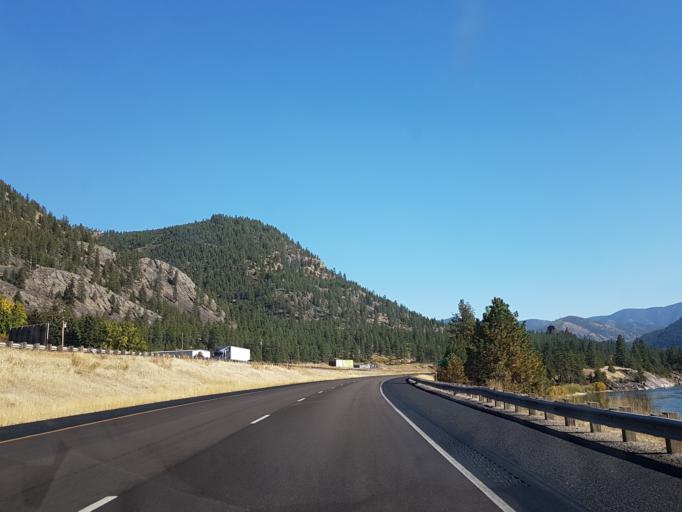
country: US
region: Montana
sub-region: Missoula County
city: Frenchtown
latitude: 47.0186
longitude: -114.5142
